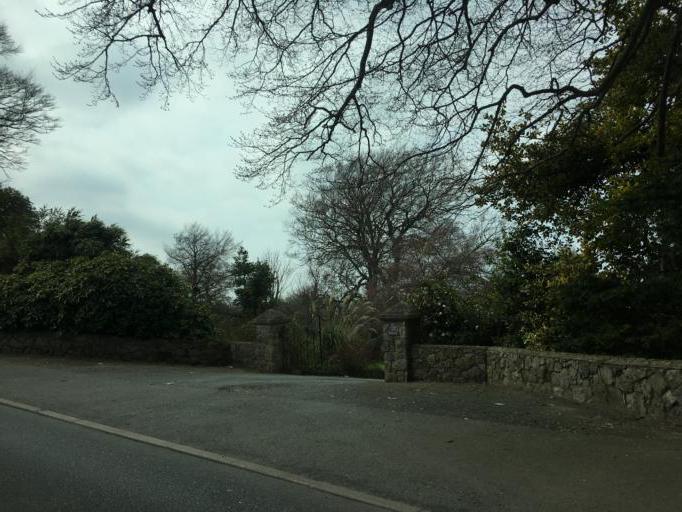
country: GB
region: Wales
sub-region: Gwynedd
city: Caernarfon
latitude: 53.1509
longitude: -4.2634
